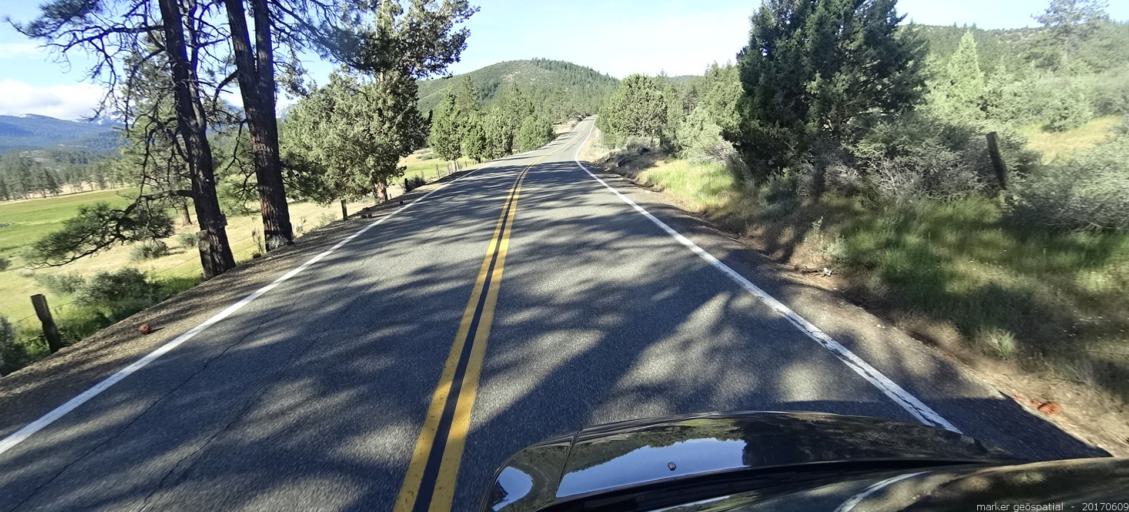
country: US
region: California
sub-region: Siskiyou County
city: Weed
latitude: 41.3559
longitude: -122.7237
